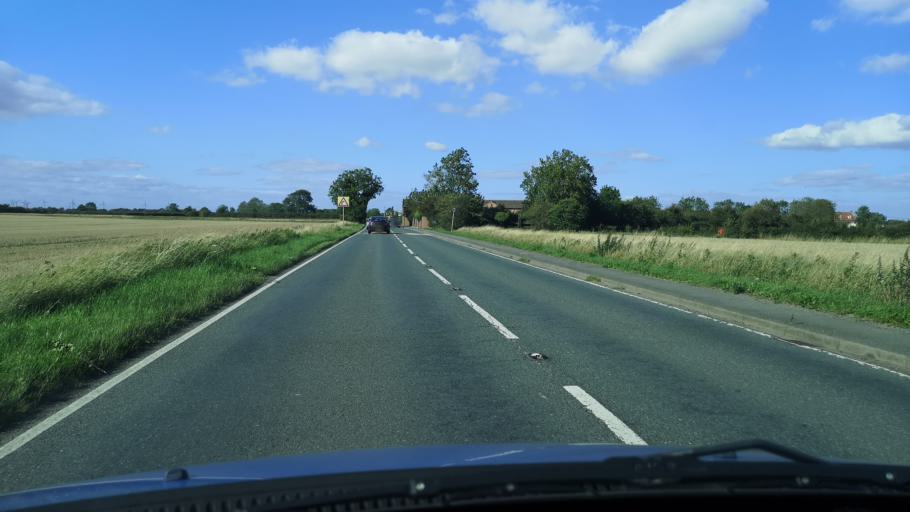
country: GB
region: England
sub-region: North Lincolnshire
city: Belton
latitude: 53.5591
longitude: -0.8177
